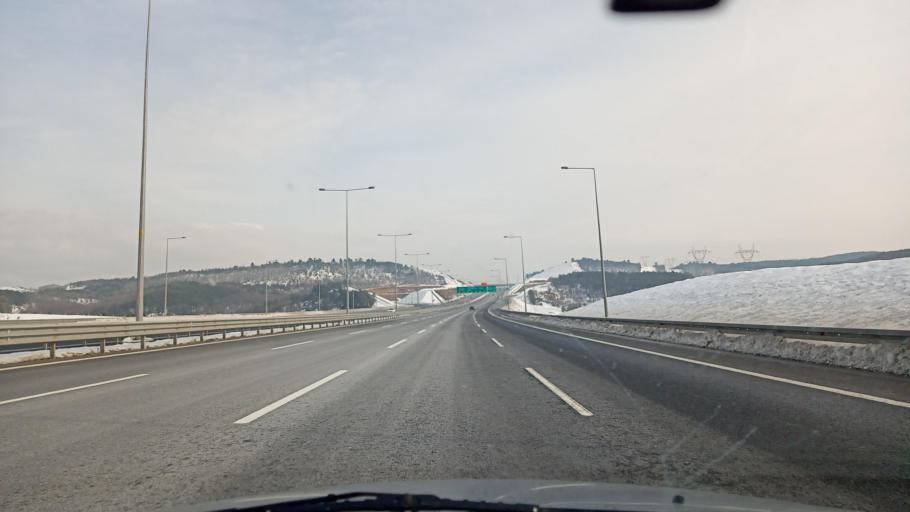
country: TR
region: Kocaeli
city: Mollafeneri
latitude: 40.9227
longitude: 29.4596
